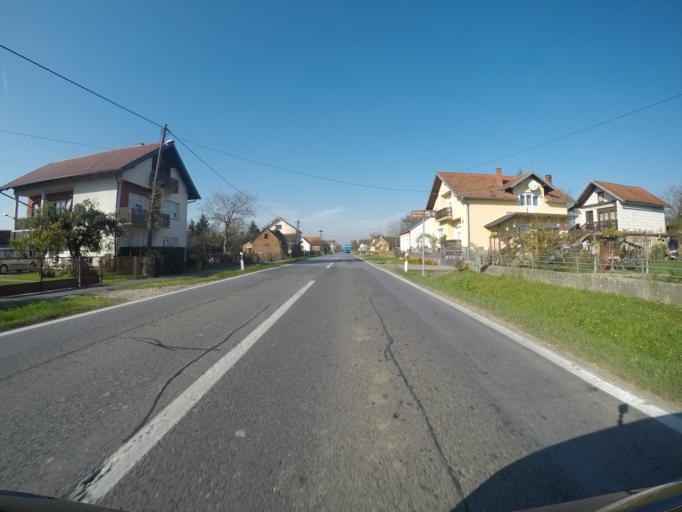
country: HR
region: Bjelovarsko-Bilogorska
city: Predavac
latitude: 45.9256
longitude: 16.7875
